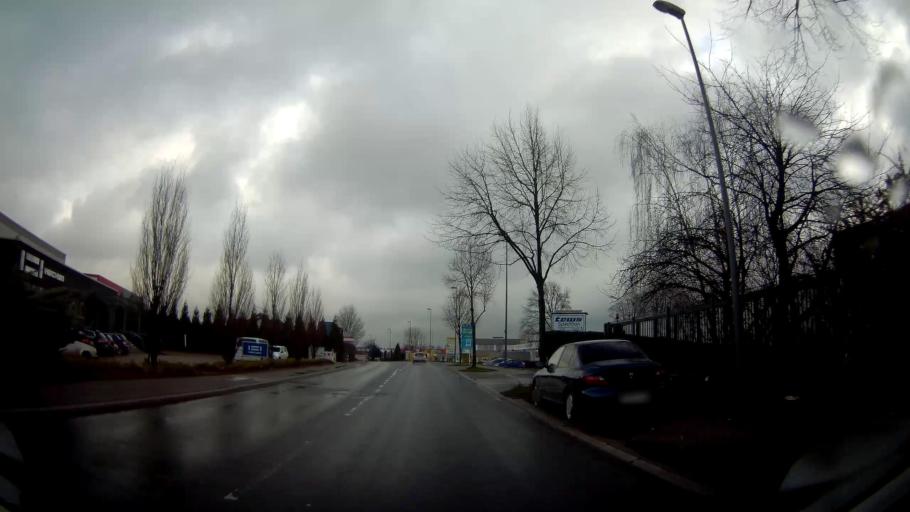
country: DE
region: North Rhine-Westphalia
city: Castrop-Rauxel
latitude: 51.5086
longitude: 7.2775
